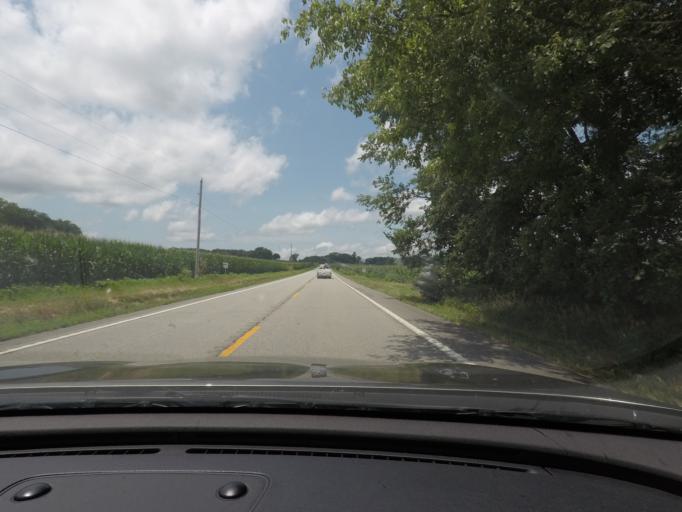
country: US
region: Missouri
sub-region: Carroll County
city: Carrollton
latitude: 39.2006
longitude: -93.4368
